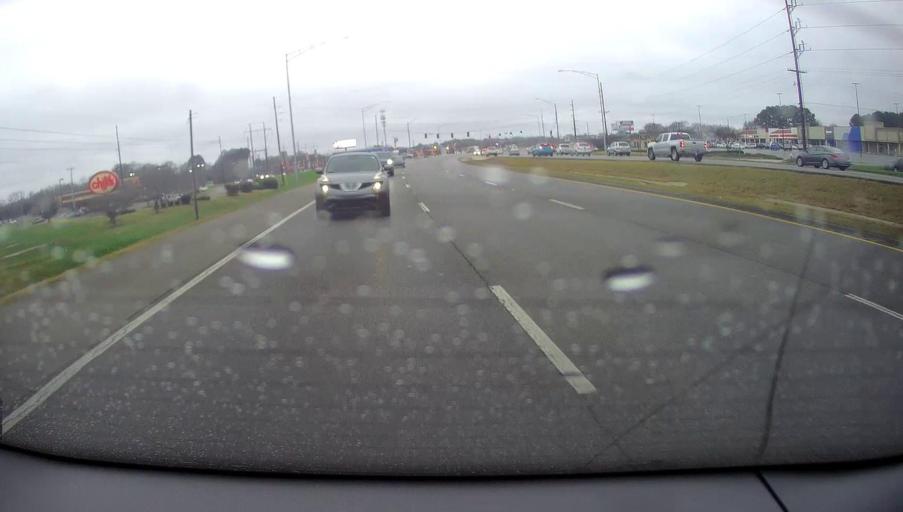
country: US
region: Alabama
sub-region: Morgan County
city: Flint City
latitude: 34.5601
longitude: -87.0036
